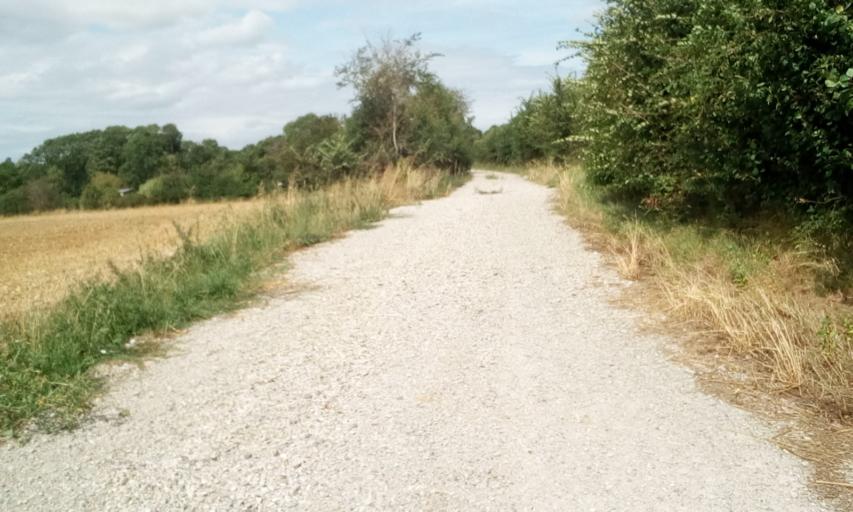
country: FR
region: Lower Normandy
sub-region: Departement du Calvados
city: Amfreville
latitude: 49.2355
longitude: -0.2310
